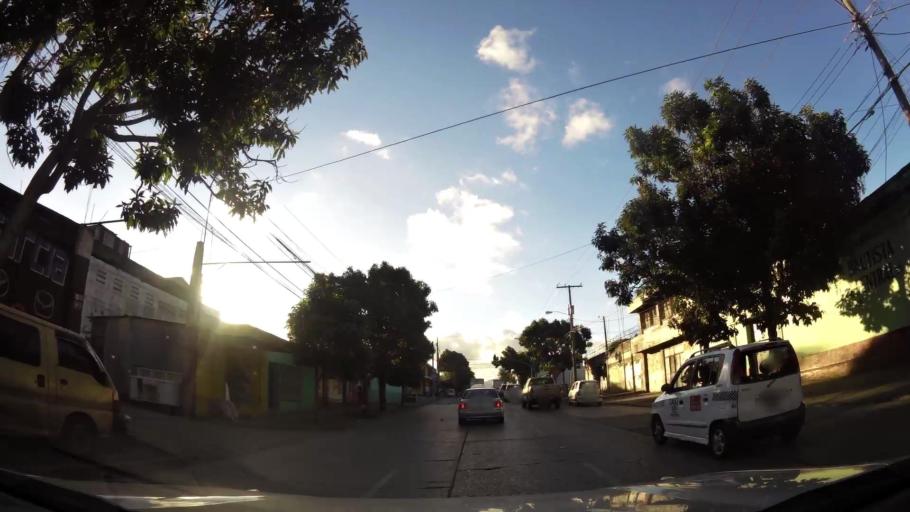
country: GT
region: Guatemala
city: Guatemala City
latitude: 14.6265
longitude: -90.5214
